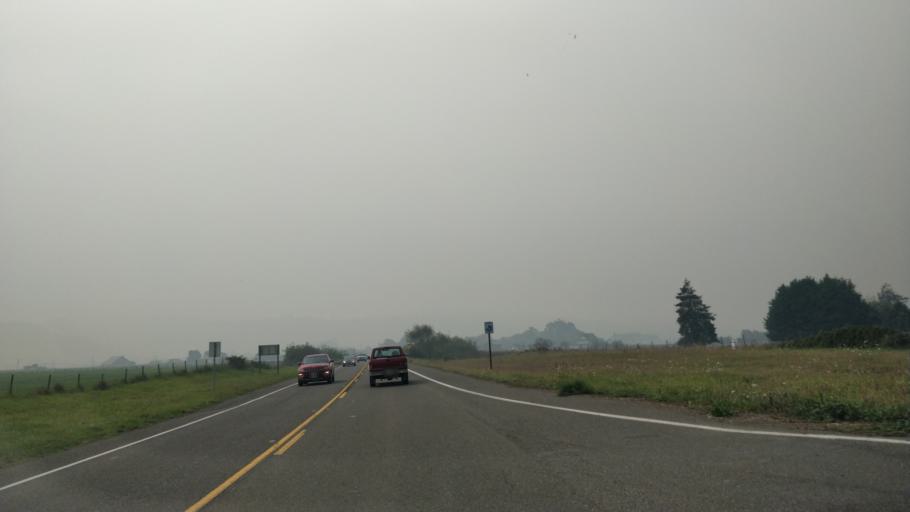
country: US
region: California
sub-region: Humboldt County
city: Ferndale
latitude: 40.5944
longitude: -124.2486
